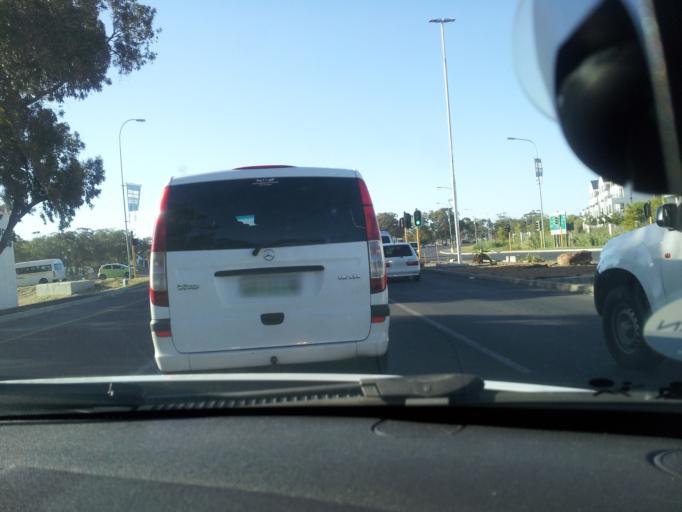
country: ZA
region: Western Cape
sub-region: Cape Winelands District Municipality
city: Stellenbosch
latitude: -34.0925
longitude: 18.8200
